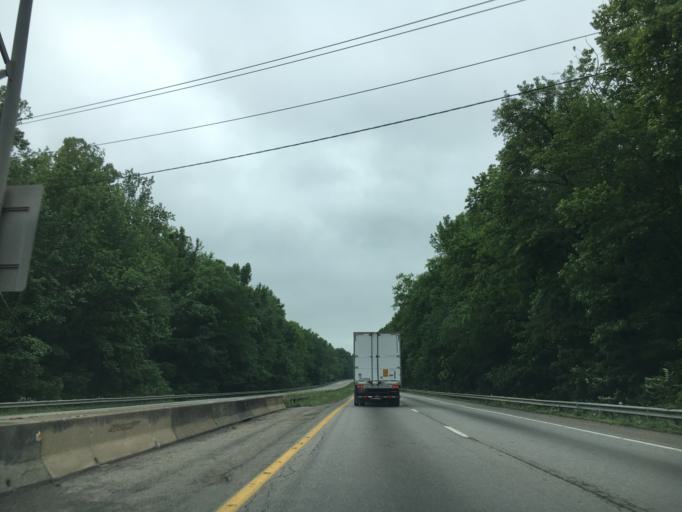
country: US
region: Virginia
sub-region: City of Petersburg
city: Petersburg
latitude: 37.2134
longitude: -77.3981
